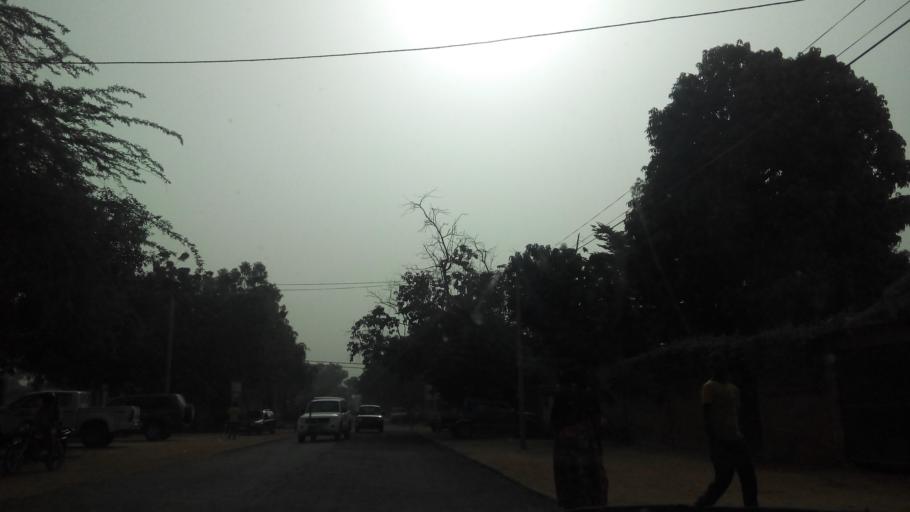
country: NE
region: Niamey
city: Niamey
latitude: 13.5215
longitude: 2.0963
